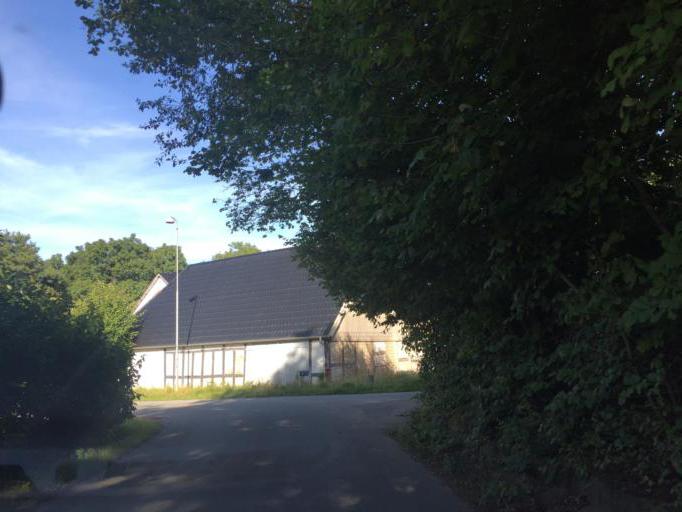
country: DK
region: South Denmark
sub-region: Odense Kommune
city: Neder Holluf
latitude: 55.3729
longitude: 10.4379
